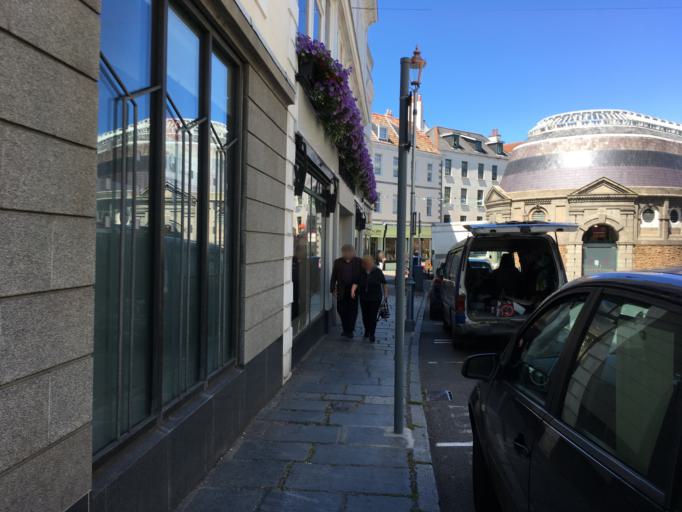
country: GG
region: St Peter Port
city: Saint Peter Port
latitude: 49.4535
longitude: -2.5383
